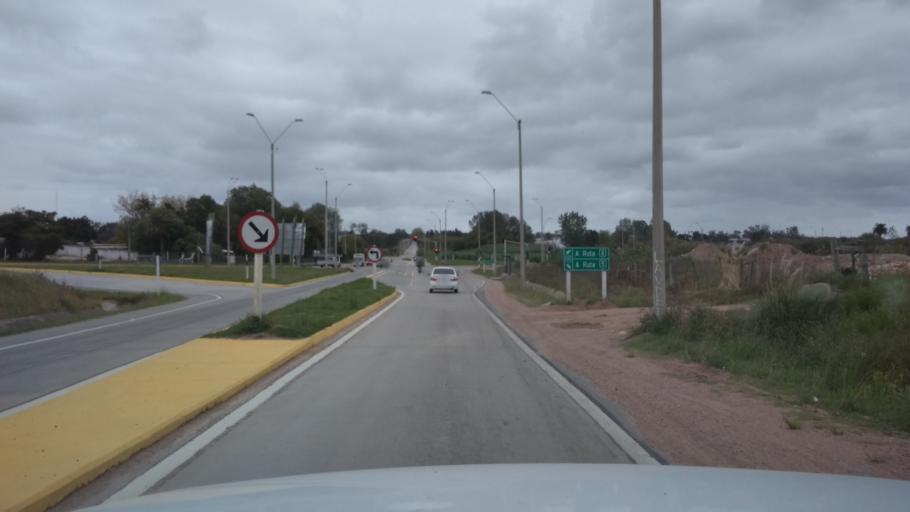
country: UY
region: Canelones
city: Toledo
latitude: -34.7961
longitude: -56.1515
